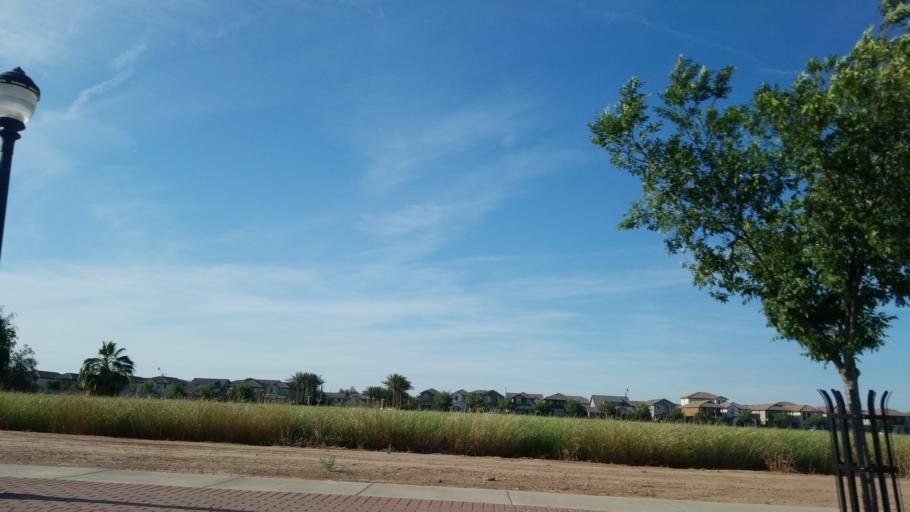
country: US
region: Arizona
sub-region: Maricopa County
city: Queen Creek
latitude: 33.3072
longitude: -111.6993
